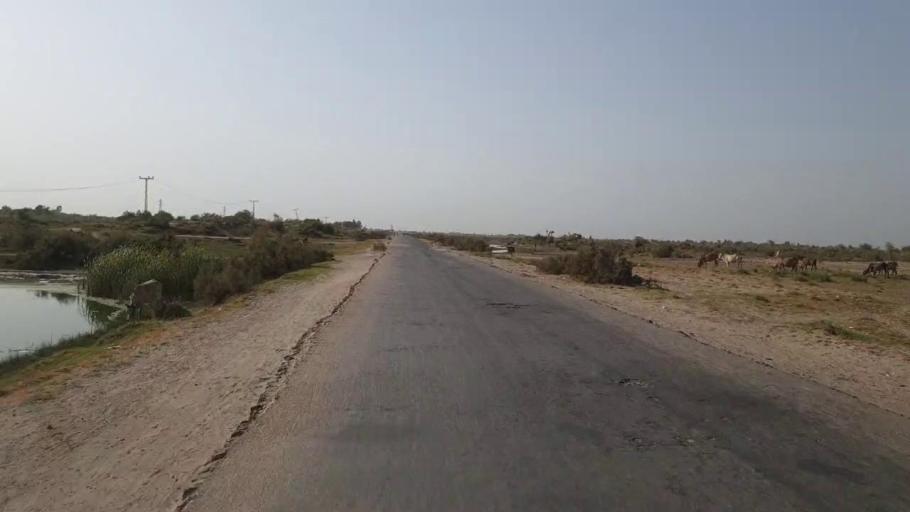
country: PK
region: Sindh
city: Khadro
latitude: 26.3394
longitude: 68.9267
